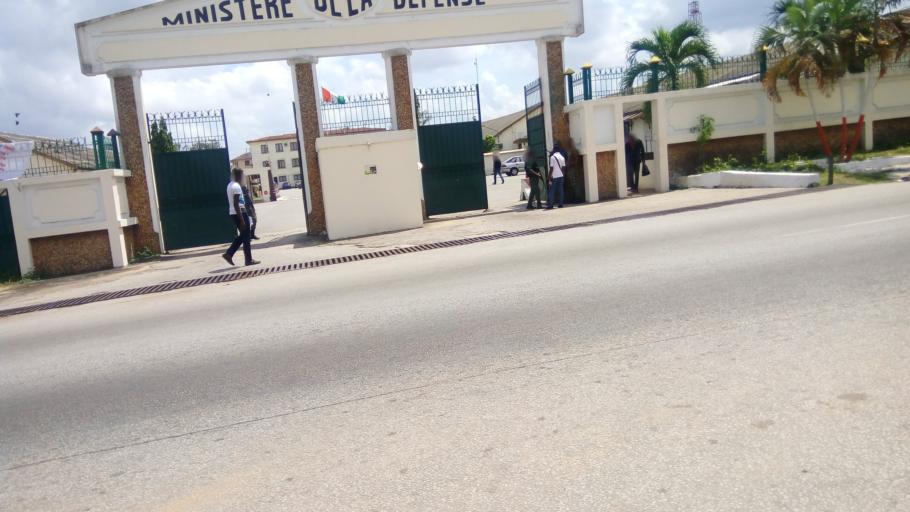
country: CI
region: Lagunes
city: Abidjan
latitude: 5.3379
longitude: -4.0237
